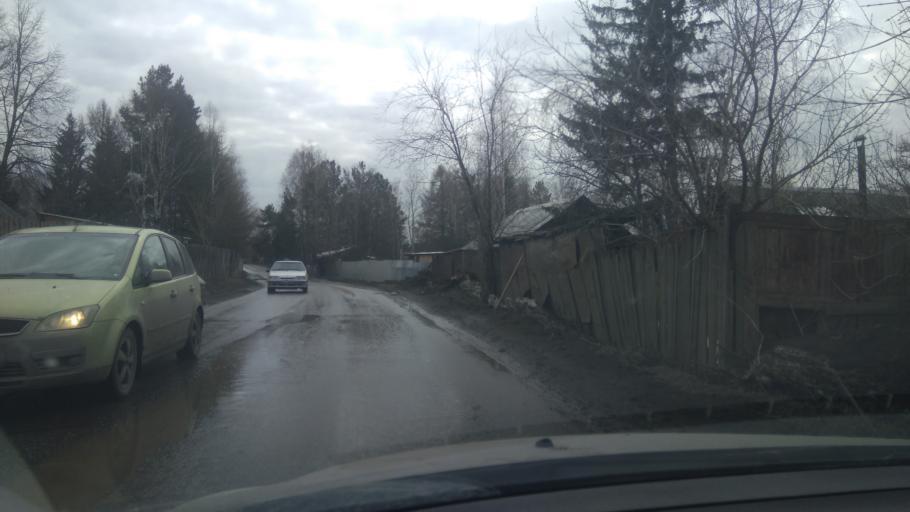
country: RU
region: Sverdlovsk
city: Severka
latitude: 56.8486
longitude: 60.3837
